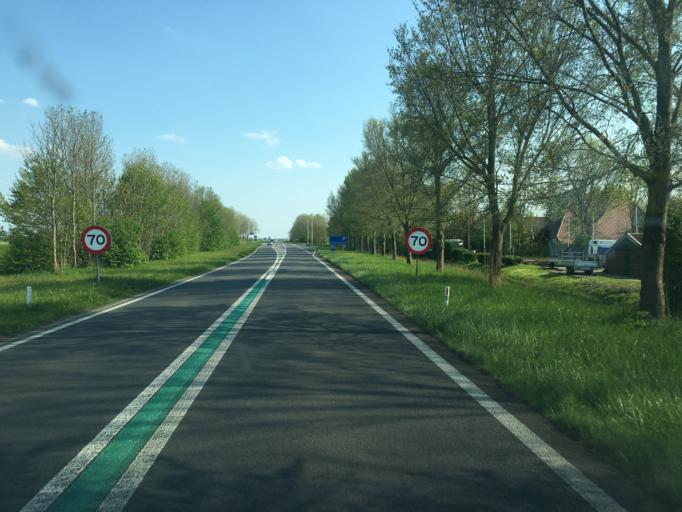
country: NL
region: Friesland
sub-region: Sudwest Fryslan
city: Workum
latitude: 52.9502
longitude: 5.4336
